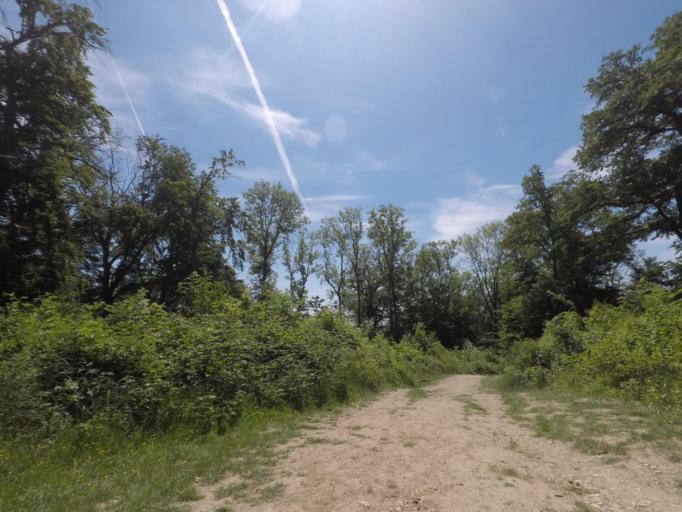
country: AT
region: Lower Austria
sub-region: Politischer Bezirk Modling
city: Perchtoldsdorf
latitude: 48.1811
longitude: 16.2469
